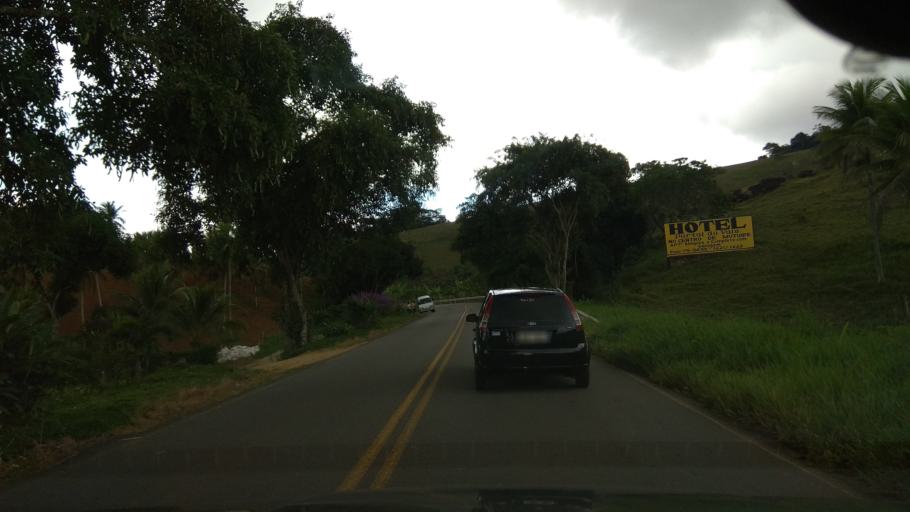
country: BR
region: Bahia
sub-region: Mutuipe
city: Mutuipe
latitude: -13.2412
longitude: -39.5379
